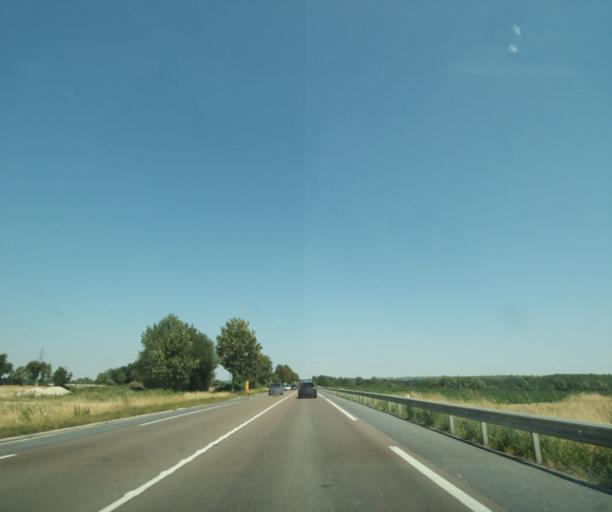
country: FR
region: Champagne-Ardenne
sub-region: Departement de la Marne
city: Frignicourt
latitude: 48.7188
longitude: 4.6322
